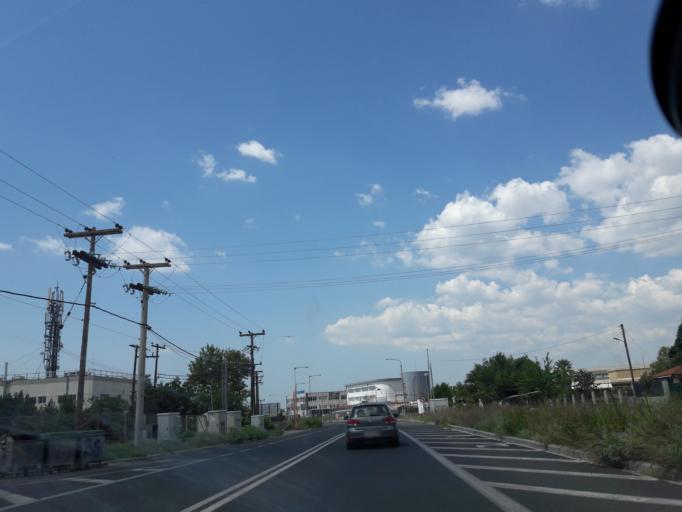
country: GR
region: Central Macedonia
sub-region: Nomos Thessalonikis
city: Thermi
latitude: 40.5405
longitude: 23.0291
